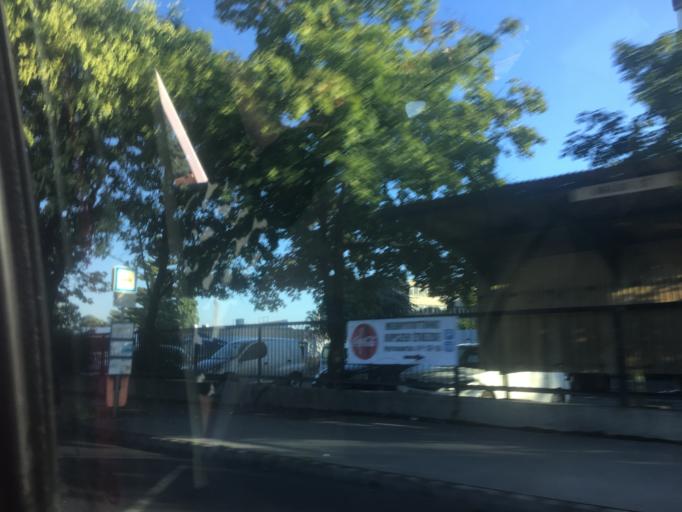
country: HU
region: Budapest
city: Budapest X. keruelet
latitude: 47.4905
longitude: 19.1495
